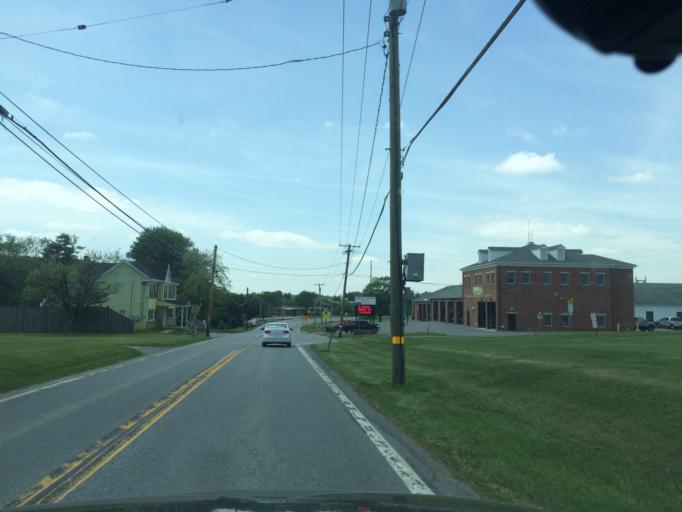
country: US
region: Maryland
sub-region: Carroll County
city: Eldersburg
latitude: 39.4680
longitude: -76.9386
